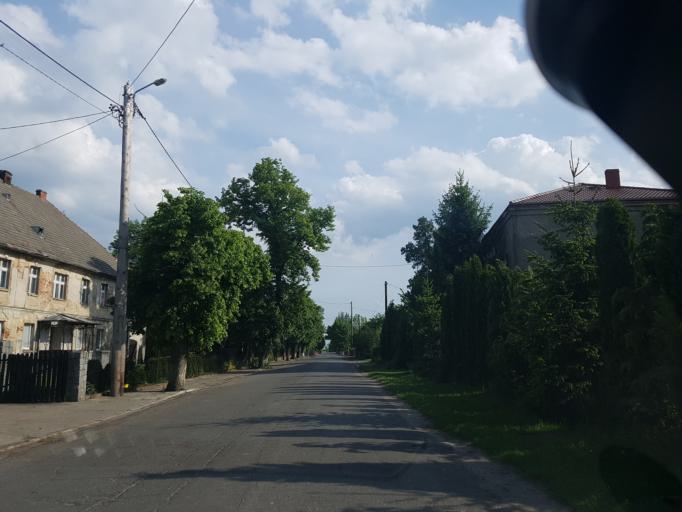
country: PL
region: Lower Silesian Voivodeship
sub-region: Powiat strzelinski
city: Wiazow
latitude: 50.8688
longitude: 17.1564
